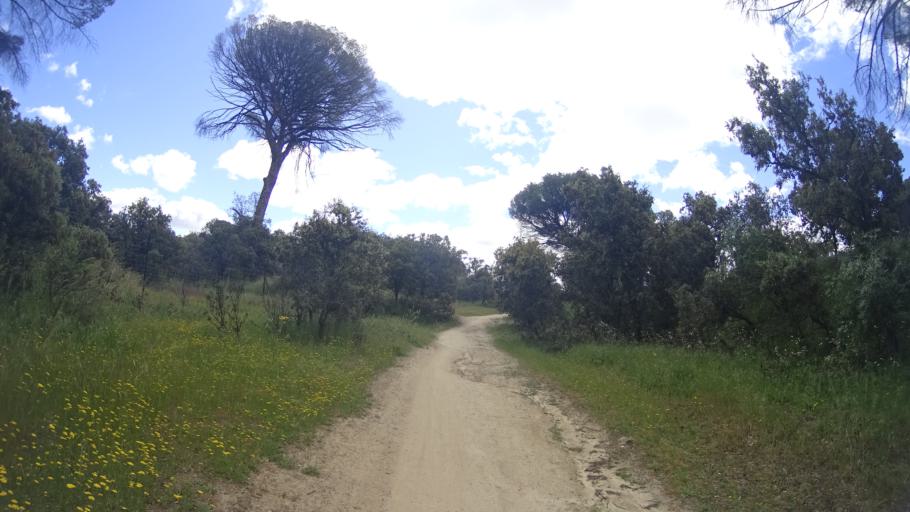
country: ES
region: Madrid
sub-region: Provincia de Madrid
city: Brunete
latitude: 40.4053
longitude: -3.9442
